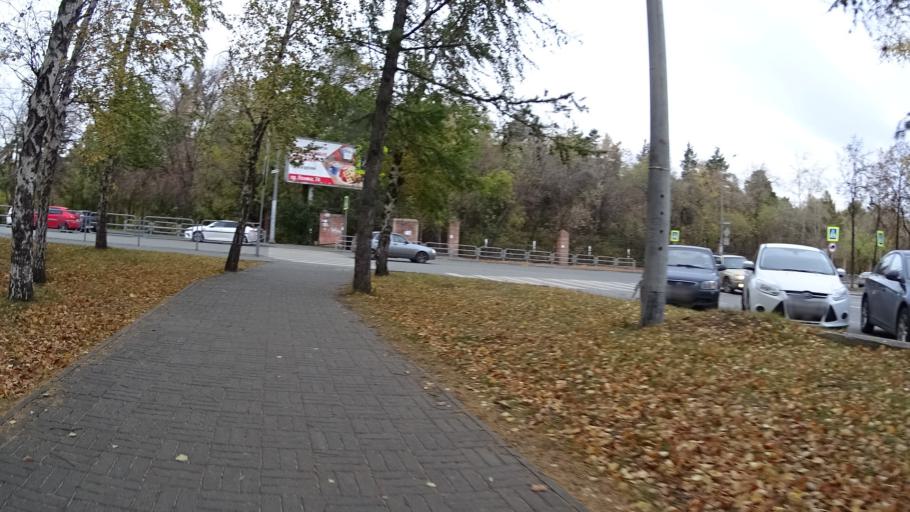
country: RU
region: Chelyabinsk
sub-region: Gorod Chelyabinsk
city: Chelyabinsk
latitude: 55.1619
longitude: 61.3751
